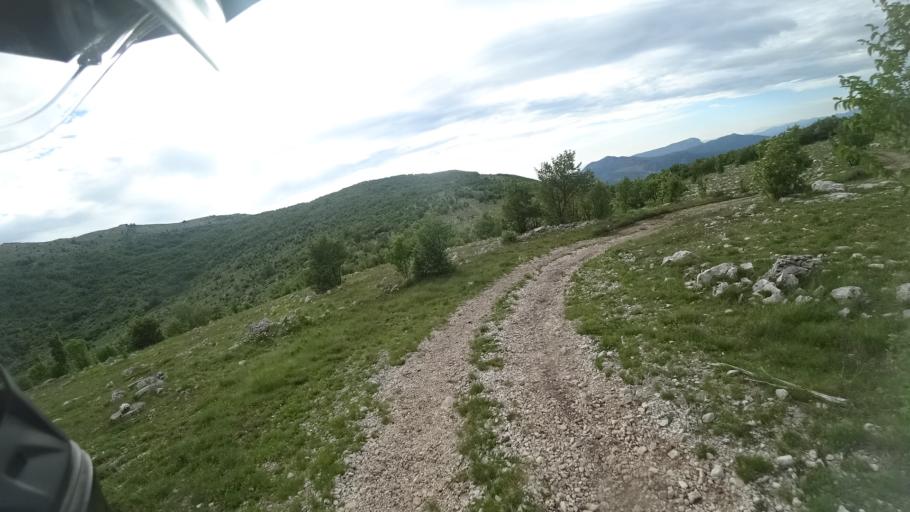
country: HR
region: Sibensko-Kniniska
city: Drnis
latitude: 43.8677
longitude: 16.3909
